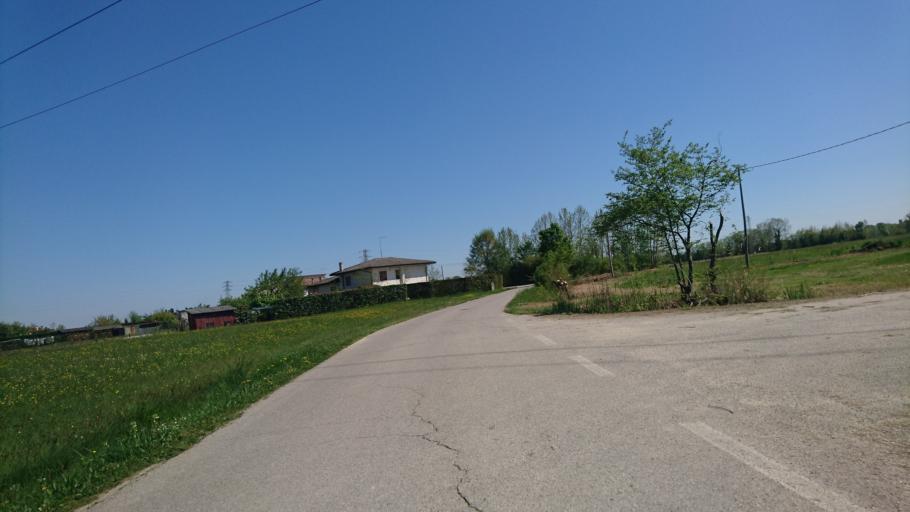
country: IT
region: Veneto
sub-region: Provincia di Treviso
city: Conscio
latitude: 45.6092
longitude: 12.2795
